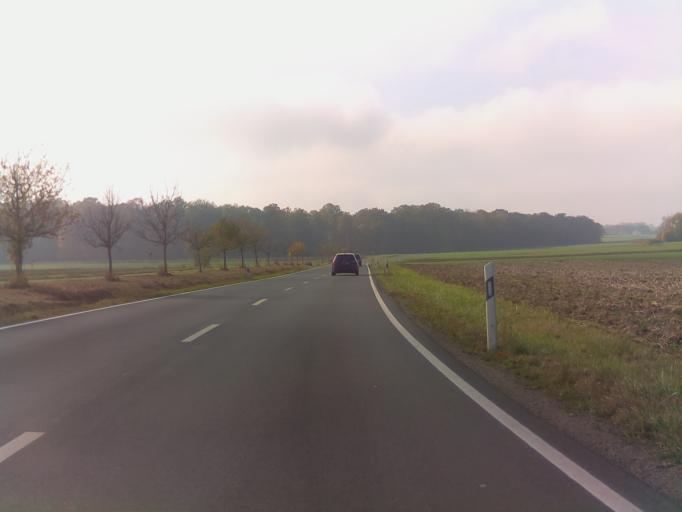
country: DE
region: Bavaria
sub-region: Regierungsbezirk Unterfranken
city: Kleinlangheim
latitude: 49.8106
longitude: 10.2867
